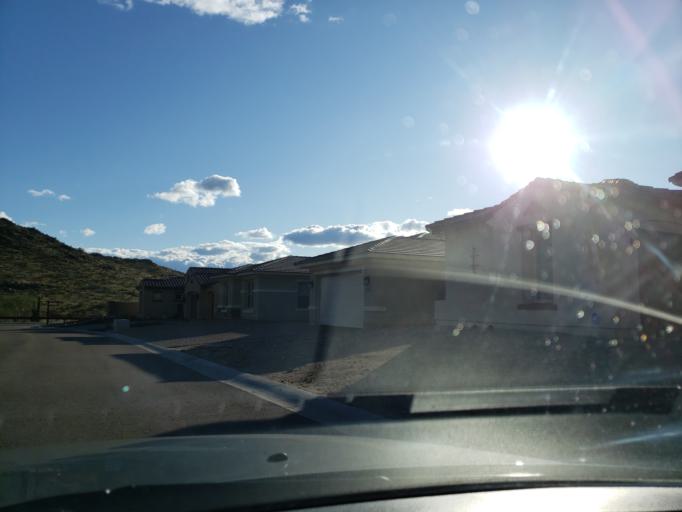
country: US
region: Arizona
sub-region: Maricopa County
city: Laveen
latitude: 33.3016
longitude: -112.1339
